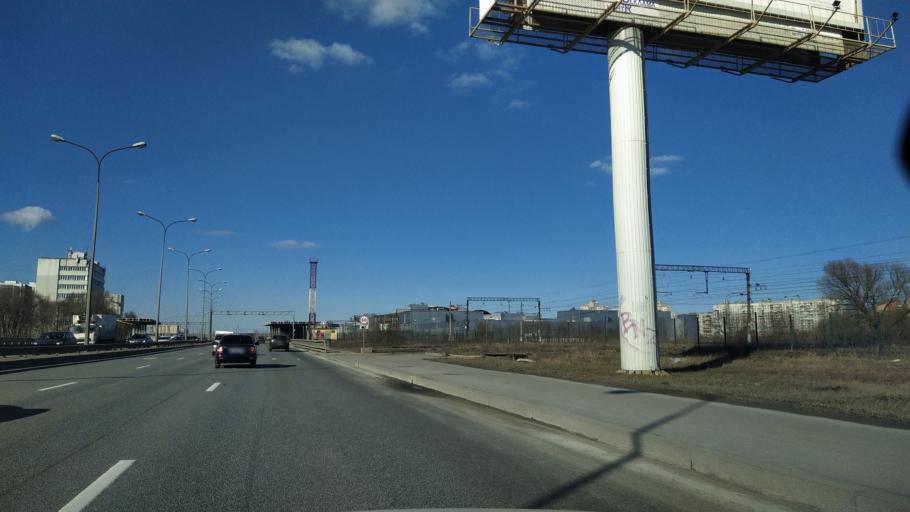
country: RU
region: St.-Petersburg
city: Shushary
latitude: 59.8212
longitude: 30.3798
